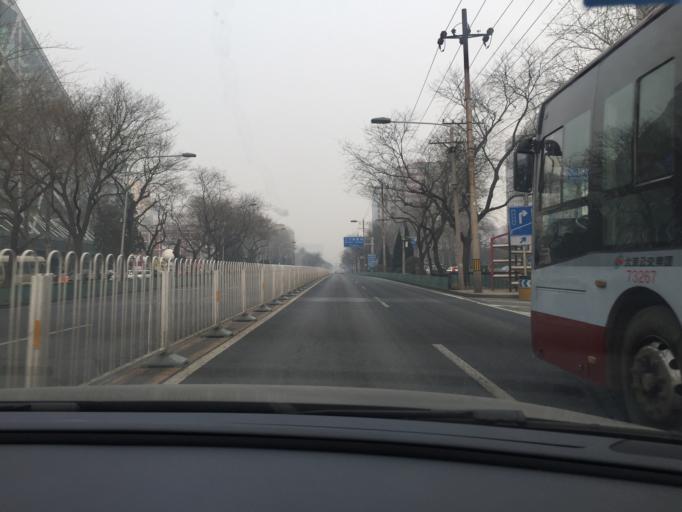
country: CN
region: Beijing
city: Chaowai
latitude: 39.9172
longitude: 116.4442
